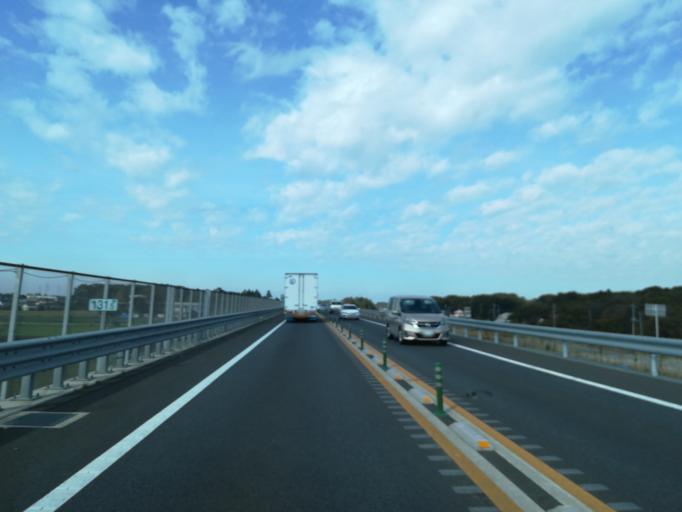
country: JP
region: Ibaraki
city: Iwai
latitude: 36.1017
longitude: 139.8657
